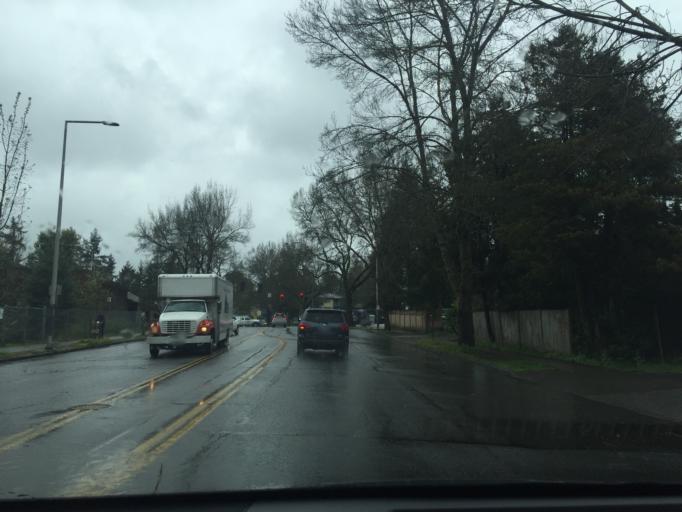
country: US
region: Washington
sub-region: King County
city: Lake Forest Park
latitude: 47.7183
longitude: -122.2911
